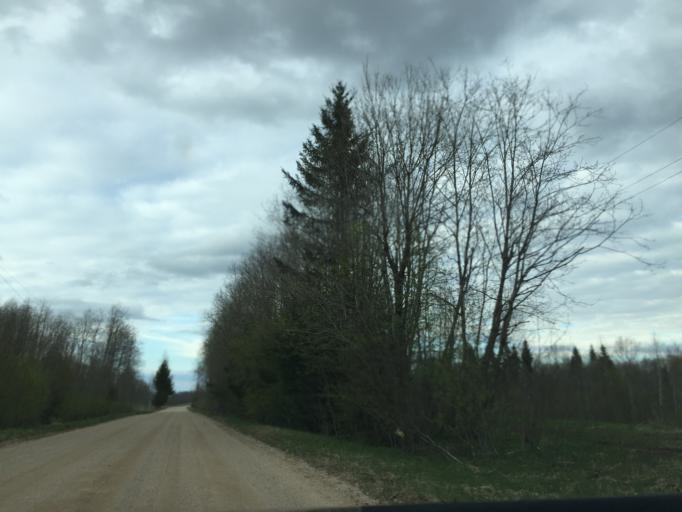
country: LV
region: Aluksnes Rajons
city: Aluksne
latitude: 57.4099
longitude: 27.0031
